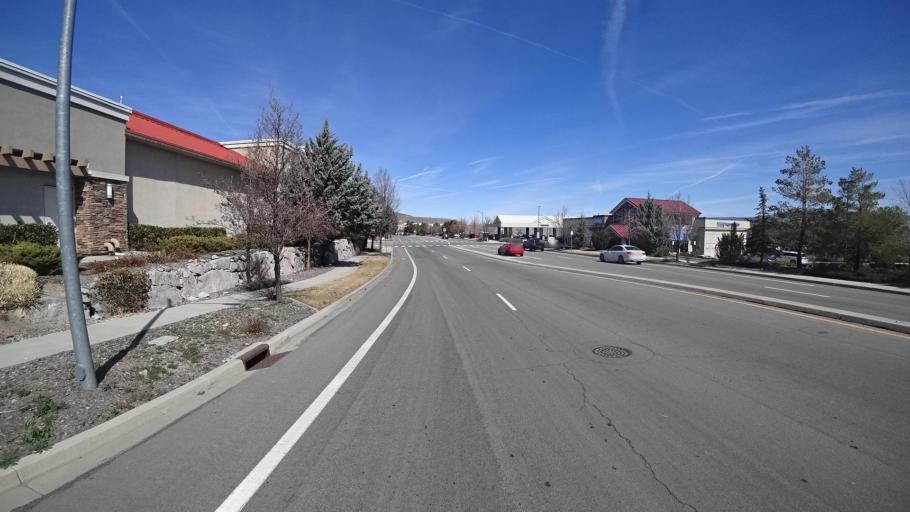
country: US
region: Nevada
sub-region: Washoe County
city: Sun Valley
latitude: 39.5775
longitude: -119.7404
